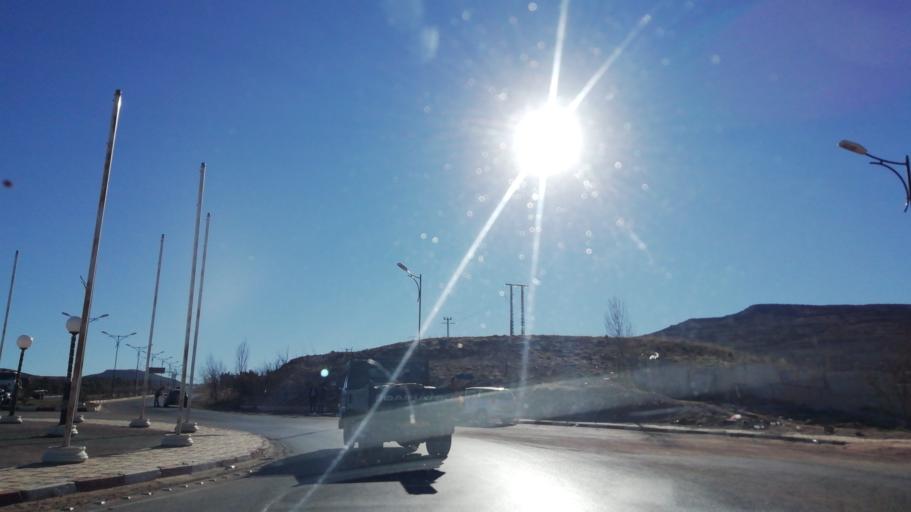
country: DZ
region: El Bayadh
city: El Bayadh
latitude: 33.6571
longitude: 1.0673
